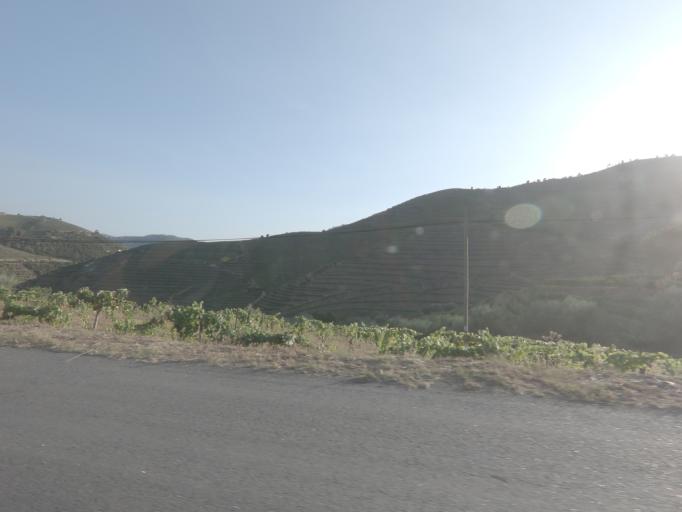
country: PT
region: Vila Real
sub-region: Sabrosa
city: Vilela
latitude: 41.1925
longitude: -7.6391
